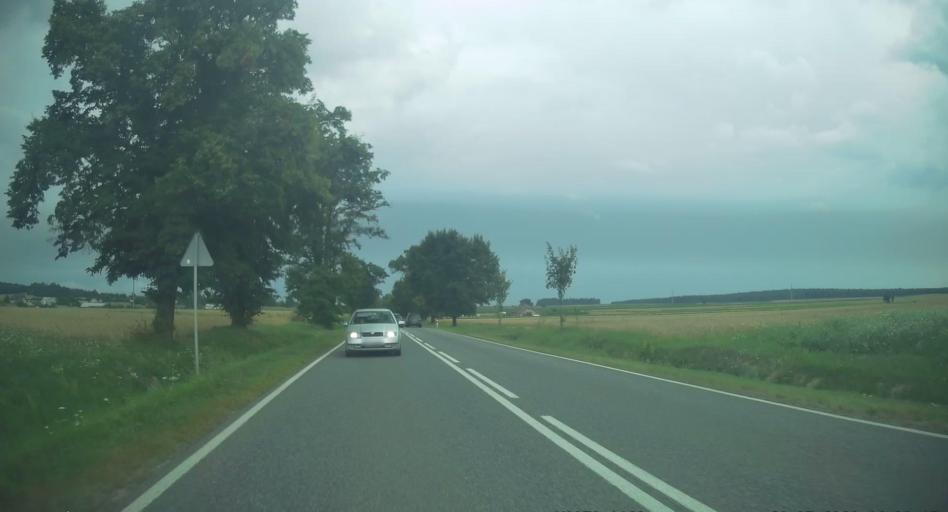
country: PL
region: Lodz Voivodeship
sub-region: Powiat skierniewicki
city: Gluchow
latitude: 51.7785
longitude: 20.0934
